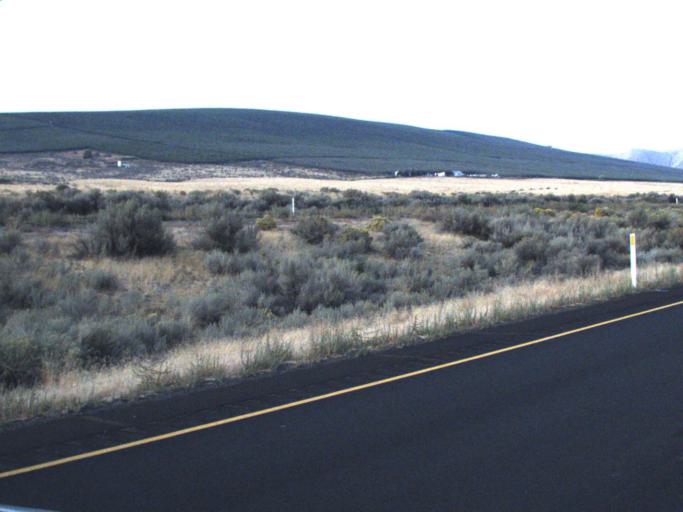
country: US
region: Washington
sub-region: Benton County
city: West Richland
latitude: 46.2620
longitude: -119.4078
